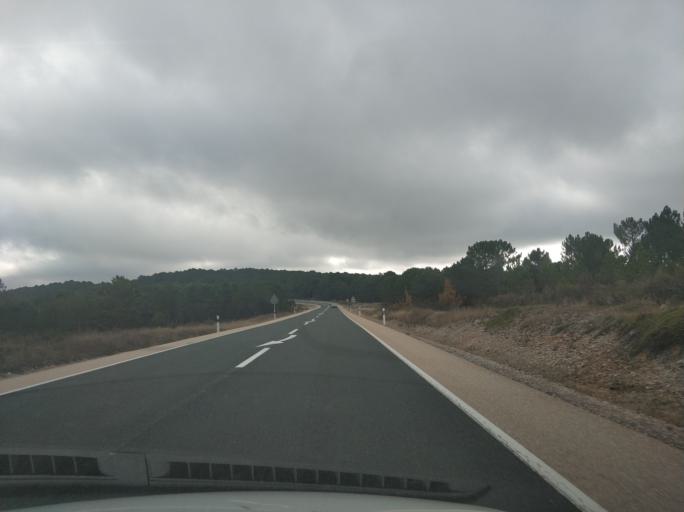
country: ES
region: Castille and Leon
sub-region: Provincia de Soria
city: Muriel Viejo
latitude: 41.8193
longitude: -2.9366
